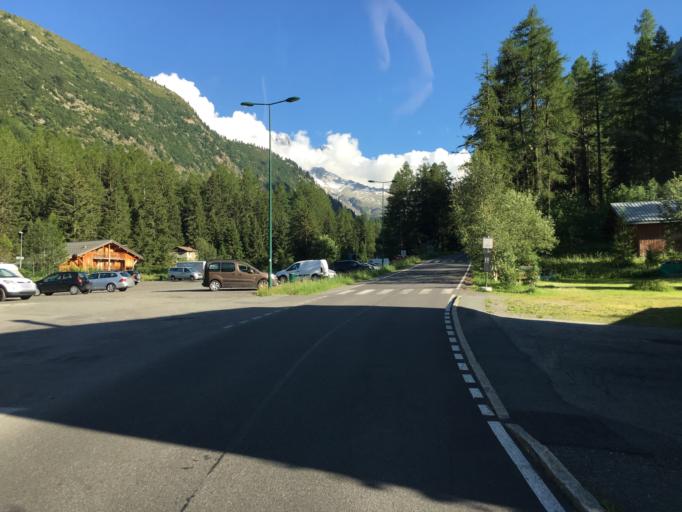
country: FR
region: Rhone-Alpes
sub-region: Departement de la Haute-Savoie
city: Chamonix-Mont-Blanc
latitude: 46.0194
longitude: 6.9196
